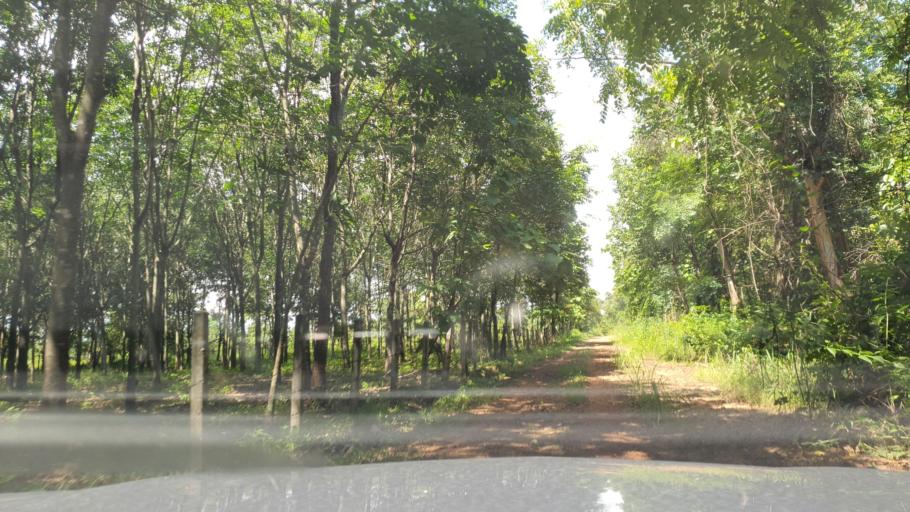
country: TH
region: Chiang Mai
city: Mae On
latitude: 18.7341
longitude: 99.2398
